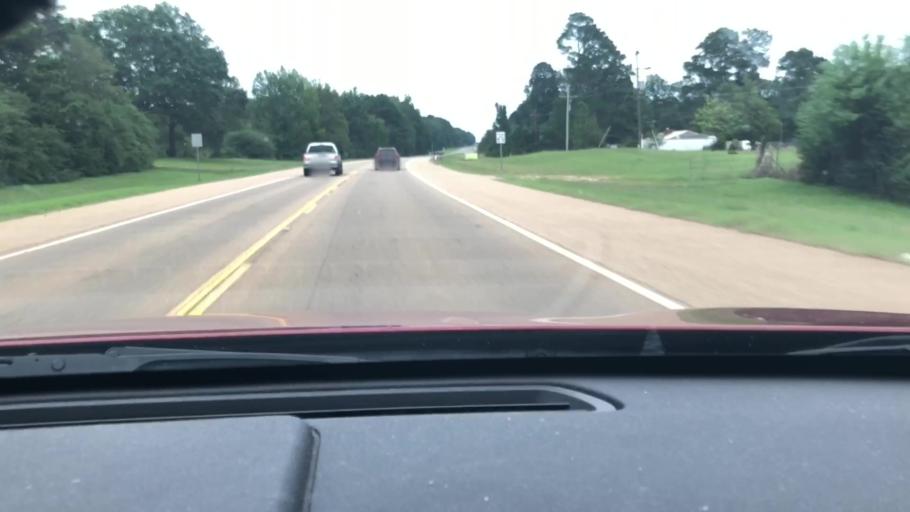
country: US
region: Arkansas
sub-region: Lafayette County
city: Stamps
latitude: 33.3649
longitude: -93.4762
